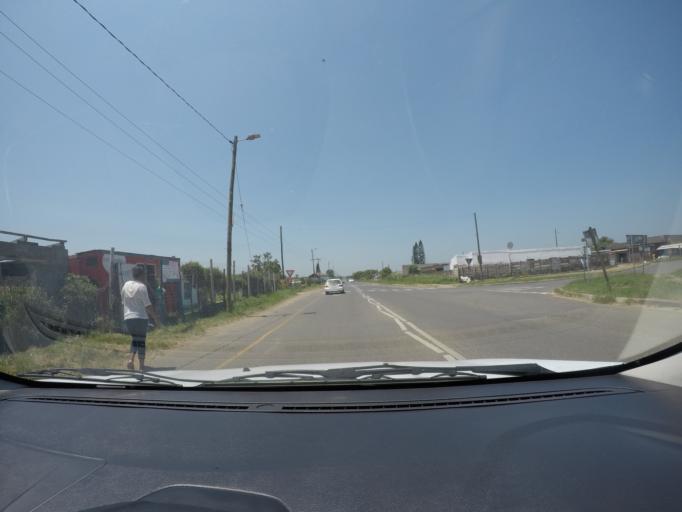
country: ZA
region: KwaZulu-Natal
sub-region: uThungulu District Municipality
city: eSikhawini
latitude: -28.8818
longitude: 31.8891
